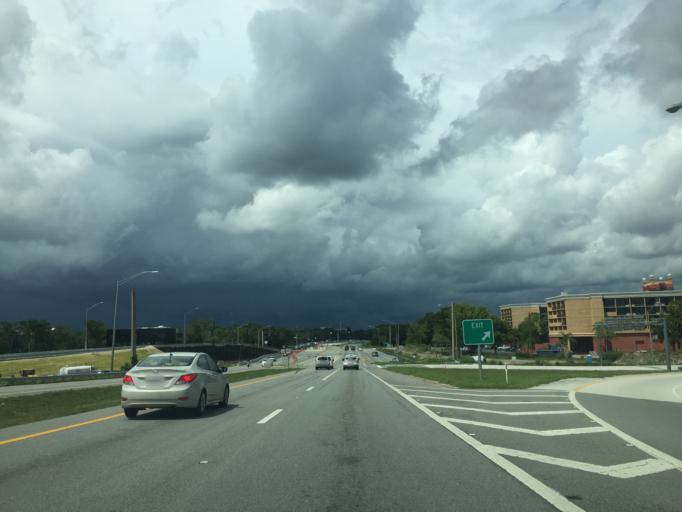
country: US
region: Florida
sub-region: Orange County
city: Eatonville
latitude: 28.6310
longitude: -81.3889
